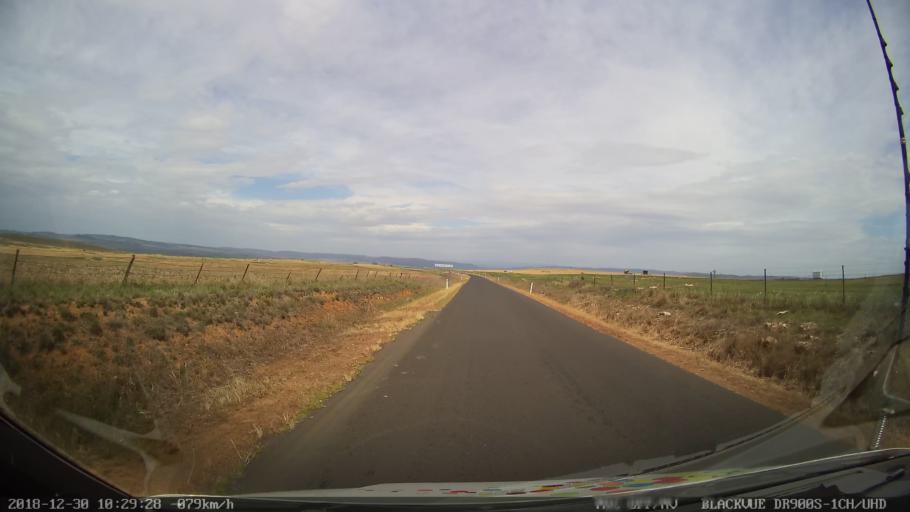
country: AU
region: New South Wales
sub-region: Snowy River
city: Berridale
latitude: -36.5014
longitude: 148.9085
